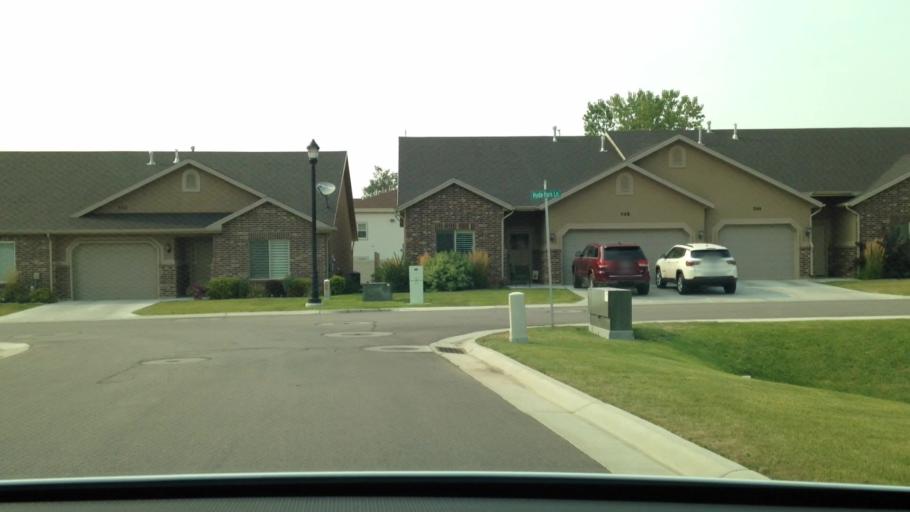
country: US
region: Utah
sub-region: Davis County
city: Kaysville
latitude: 41.0445
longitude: -111.9485
